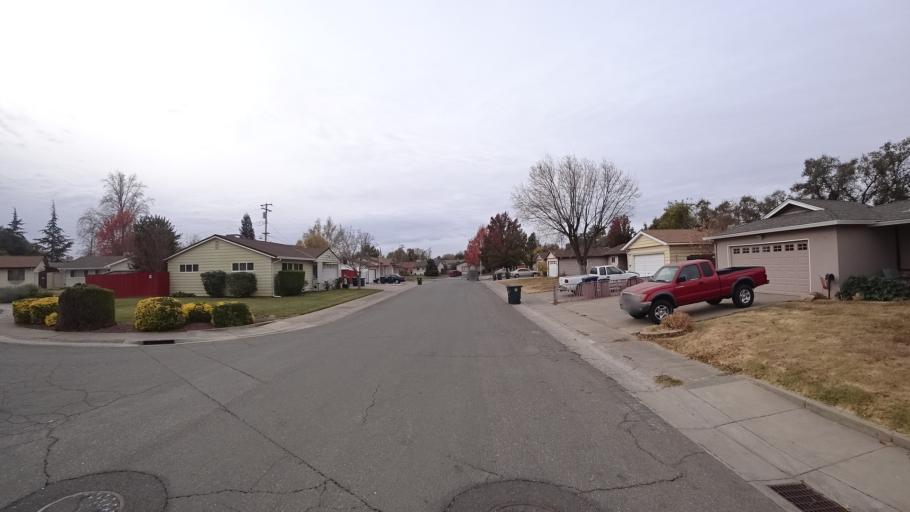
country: US
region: California
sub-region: Sacramento County
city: Citrus Heights
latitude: 38.7128
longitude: -121.3024
